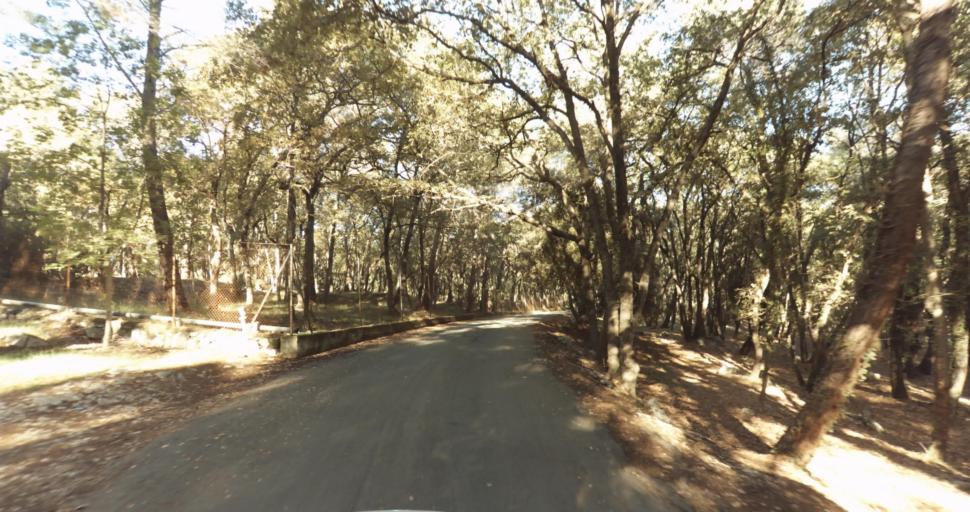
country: FR
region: Provence-Alpes-Cote d'Azur
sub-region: Departement des Alpes-Maritimes
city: Vence
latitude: 43.7111
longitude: 7.0948
